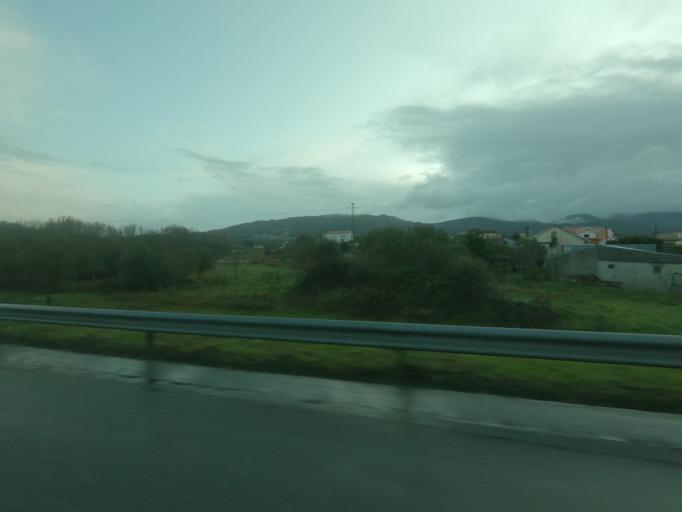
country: PT
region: Viana do Castelo
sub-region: Valenca
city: Valenza
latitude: 42.0089
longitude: -8.6471
